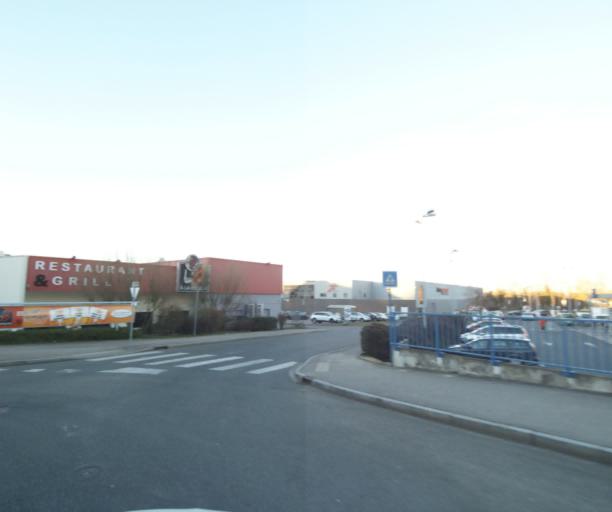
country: FR
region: Lorraine
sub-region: Departement de Meurthe-et-Moselle
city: Jarville-la-Malgrange
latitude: 48.6681
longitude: 6.2087
